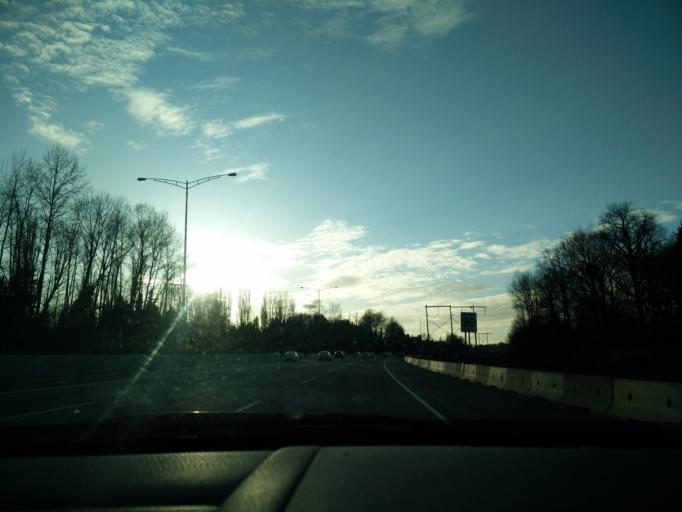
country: CA
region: British Columbia
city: Burnaby
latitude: 49.2373
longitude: -122.9431
